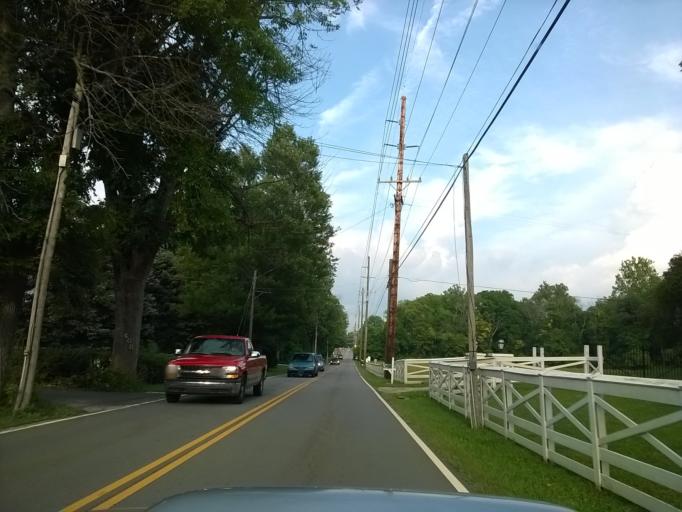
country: US
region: Indiana
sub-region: Hamilton County
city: Carmel
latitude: 39.9855
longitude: -86.1341
